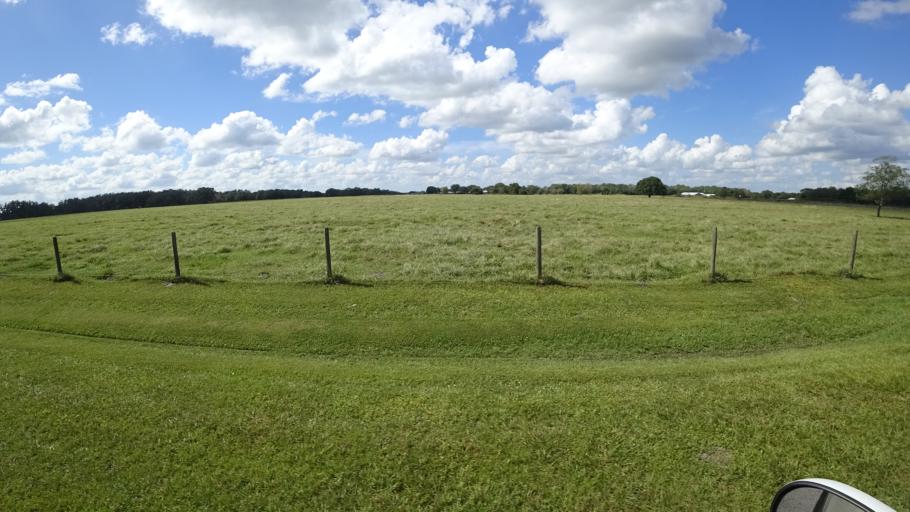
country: US
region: Florida
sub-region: Sarasota County
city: Lake Sarasota
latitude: 27.3372
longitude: -82.1545
